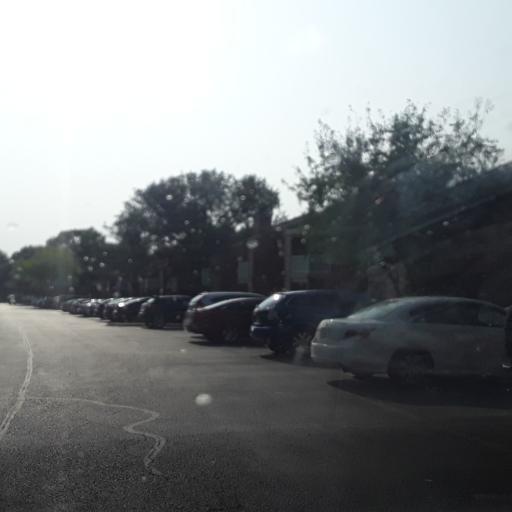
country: US
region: Tennessee
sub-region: Williamson County
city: Brentwood
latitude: 36.0540
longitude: -86.7486
